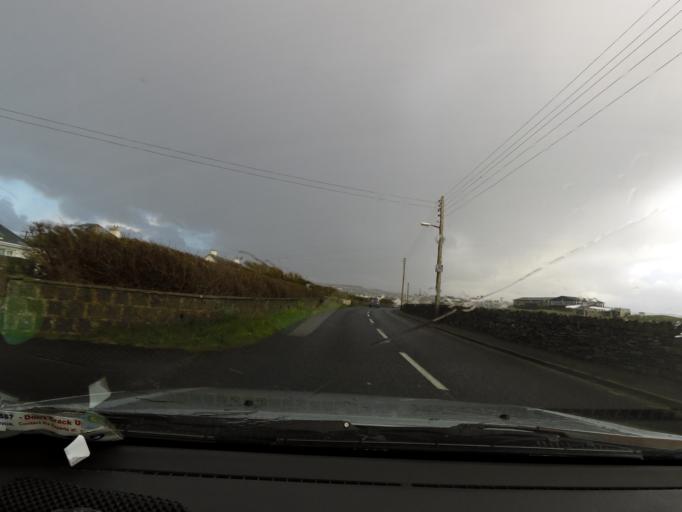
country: IE
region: Munster
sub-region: An Clar
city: Kilrush
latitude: 52.9372
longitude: -9.3460
